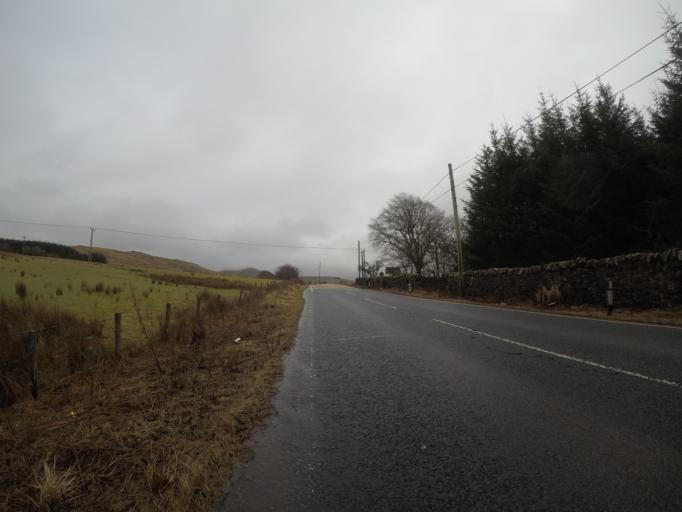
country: GB
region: Scotland
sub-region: North Ayrshire
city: Fairlie
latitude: 55.7763
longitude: -4.8208
